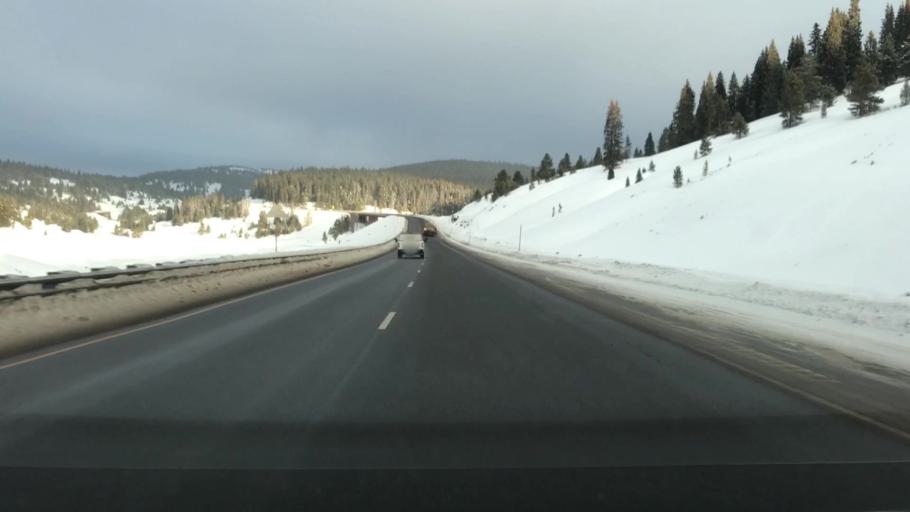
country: US
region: Colorado
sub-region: Summit County
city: Frisco
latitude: 39.5108
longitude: -106.2028
